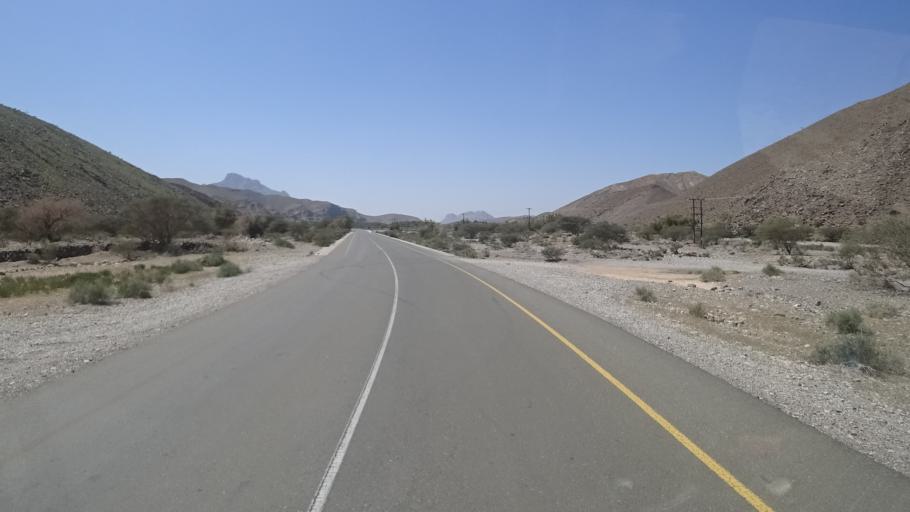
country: OM
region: Muhafazat ad Dakhiliyah
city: Bahla'
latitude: 23.2199
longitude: 56.9716
